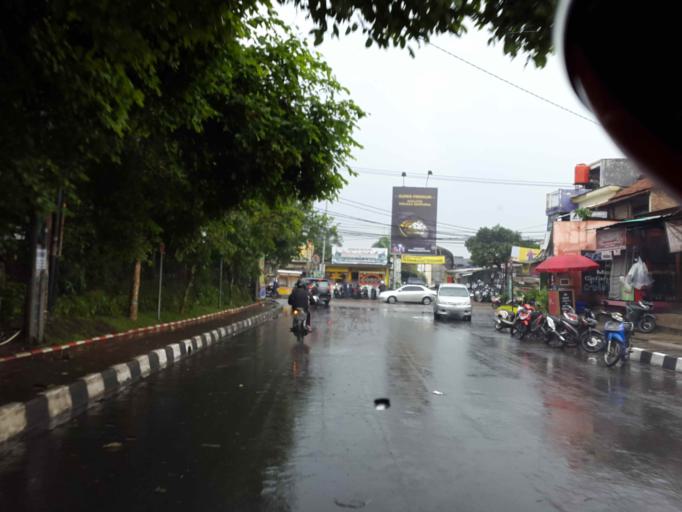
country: ID
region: West Java
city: Cimahi
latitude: -6.8724
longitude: 107.5551
